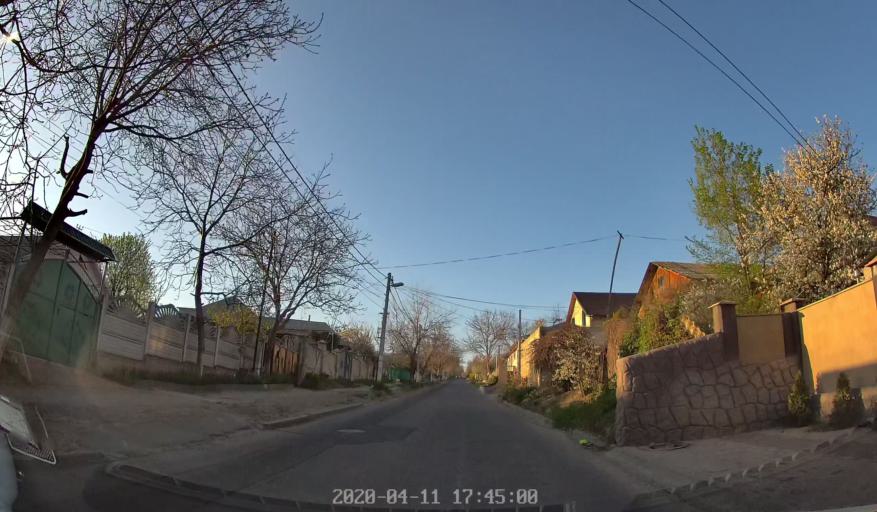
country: MD
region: Chisinau
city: Chisinau
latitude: 46.9816
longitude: 28.8232
